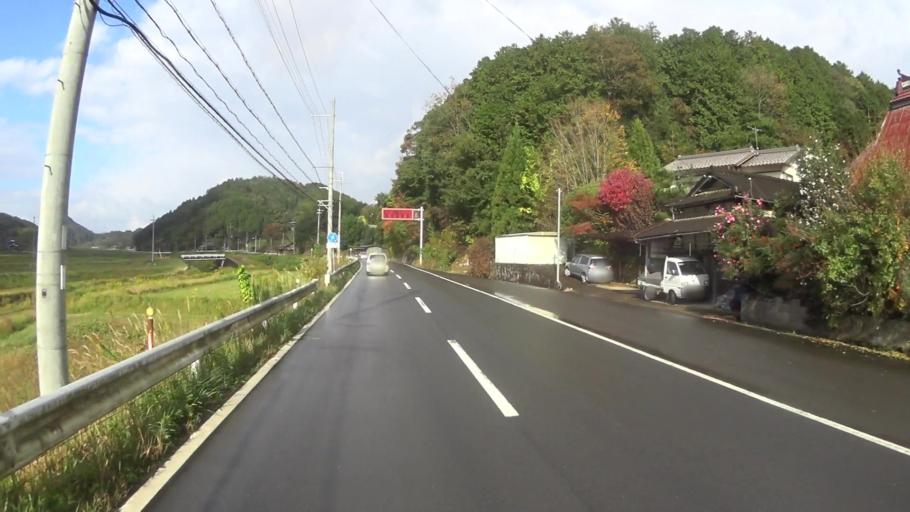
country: JP
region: Kyoto
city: Ayabe
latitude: 35.3679
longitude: 135.1959
